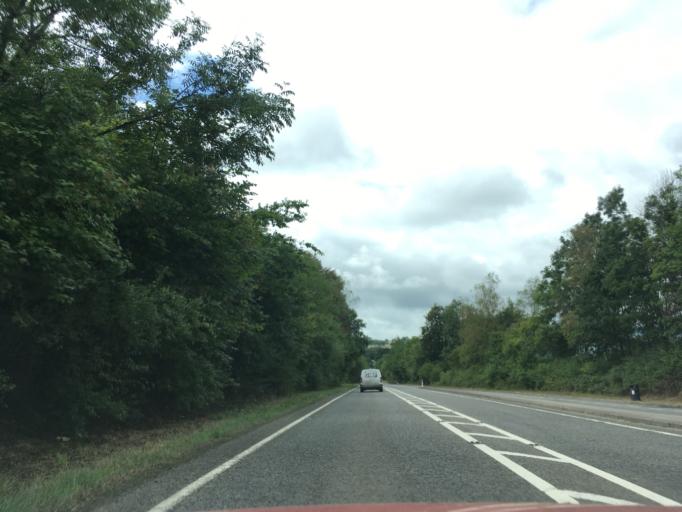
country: GB
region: Wales
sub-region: Carmarthenshire
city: Llandeilo
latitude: 51.8920
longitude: -4.0193
